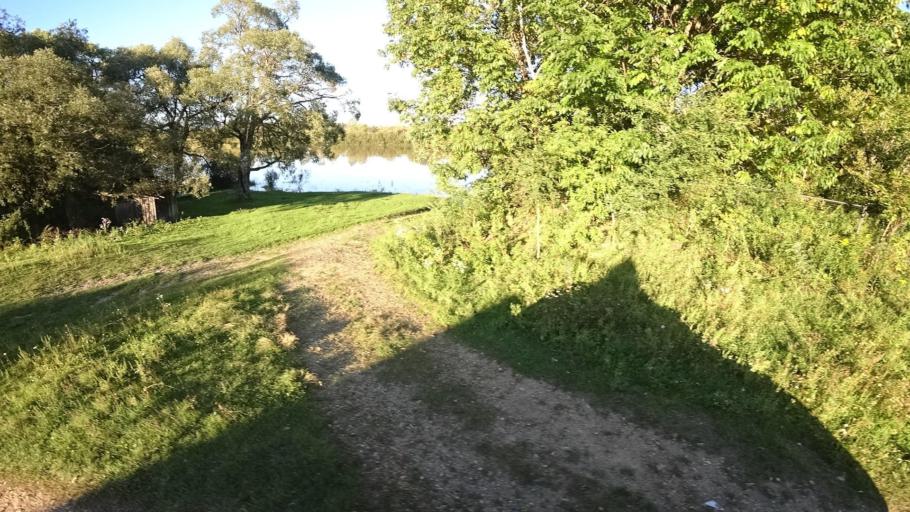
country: RU
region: Primorskiy
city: Kirovskiy
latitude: 44.8348
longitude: 133.5758
